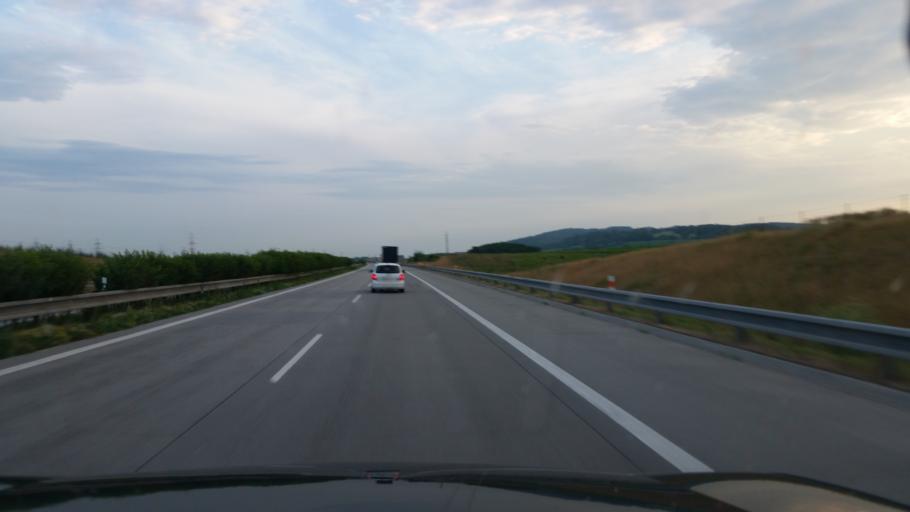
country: CZ
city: Fulnek
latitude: 49.6809
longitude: 17.9370
